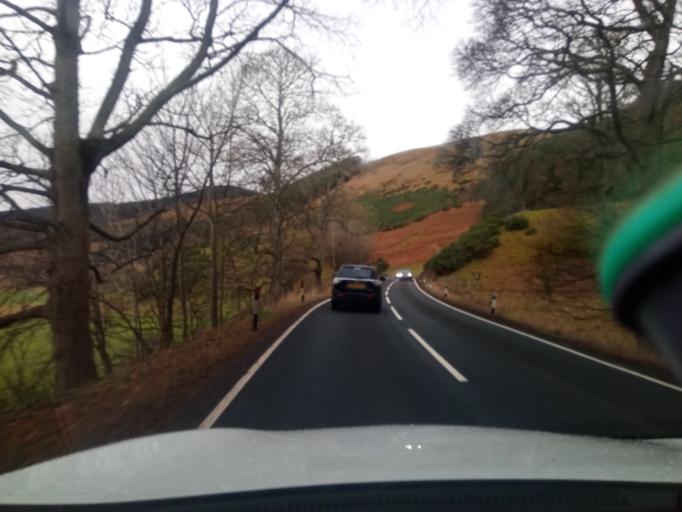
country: GB
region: Scotland
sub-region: The Scottish Borders
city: Innerleithen
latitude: 55.6281
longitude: -2.9798
